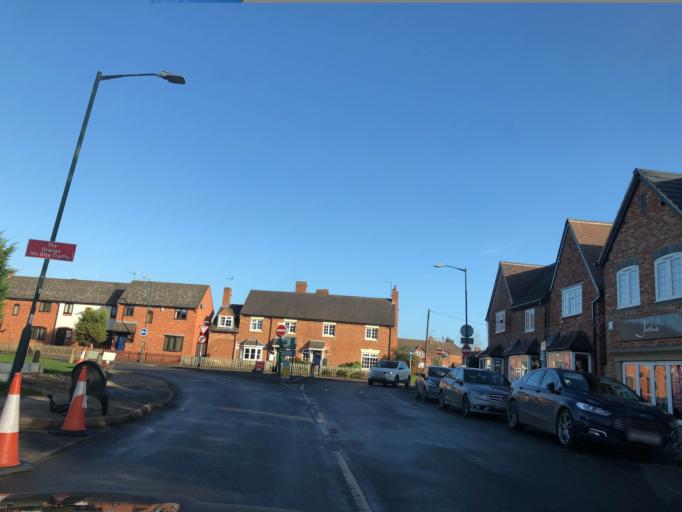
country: GB
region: England
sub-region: Warwickshire
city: Wellesbourne Mountford
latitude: 52.1961
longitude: -1.5929
